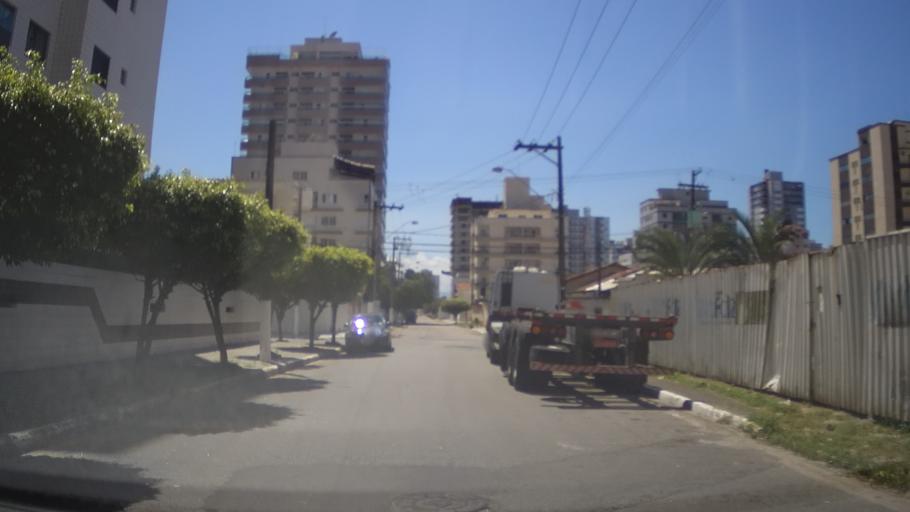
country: BR
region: Sao Paulo
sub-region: Praia Grande
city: Praia Grande
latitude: -24.0265
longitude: -46.4703
